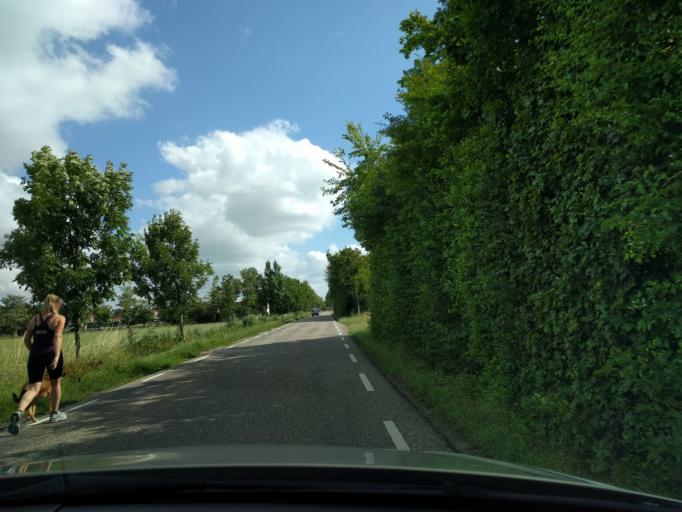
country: NL
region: Zeeland
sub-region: Gemeente Veere
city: Veere
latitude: 51.5120
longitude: 3.6759
